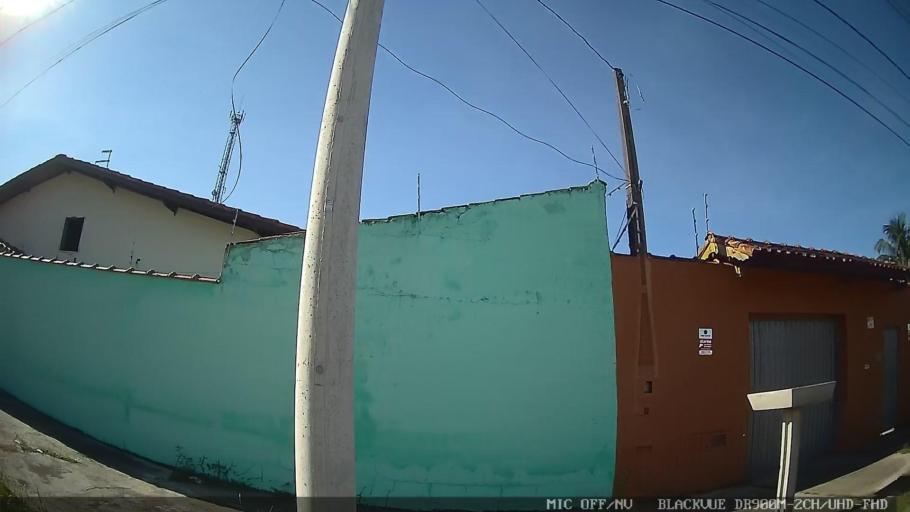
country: BR
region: Sao Paulo
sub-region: Itanhaem
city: Itanhaem
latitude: -24.2241
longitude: -46.8783
